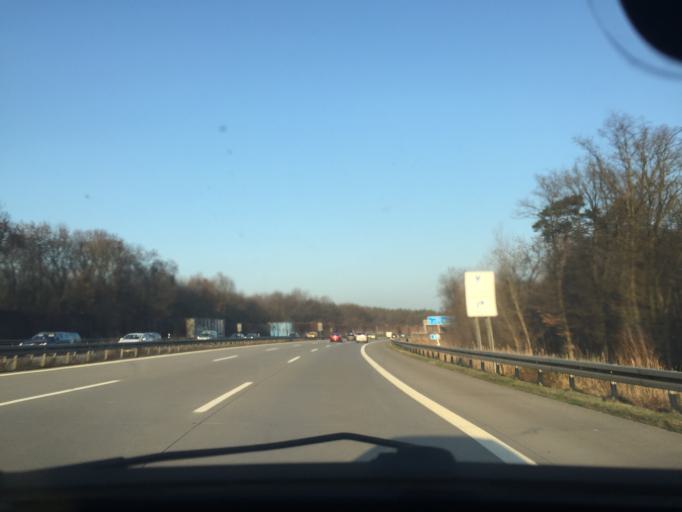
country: DE
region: Berlin
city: Wannsee
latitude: 52.3615
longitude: 13.1411
